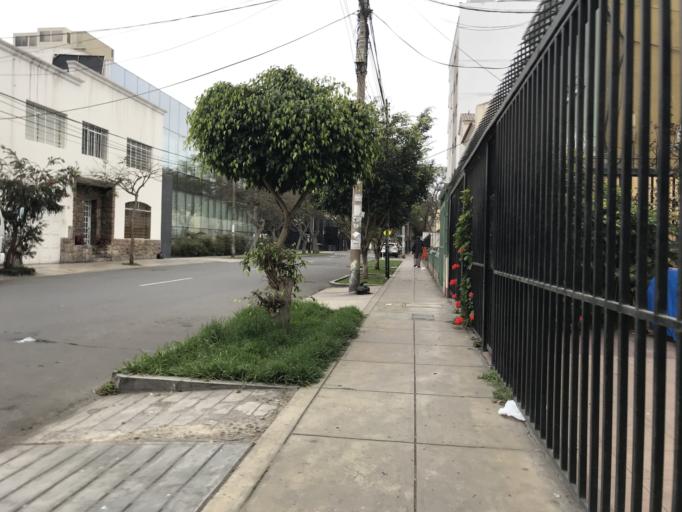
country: PE
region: Lima
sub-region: Lima
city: San Isidro
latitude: -12.0902
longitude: -77.0365
